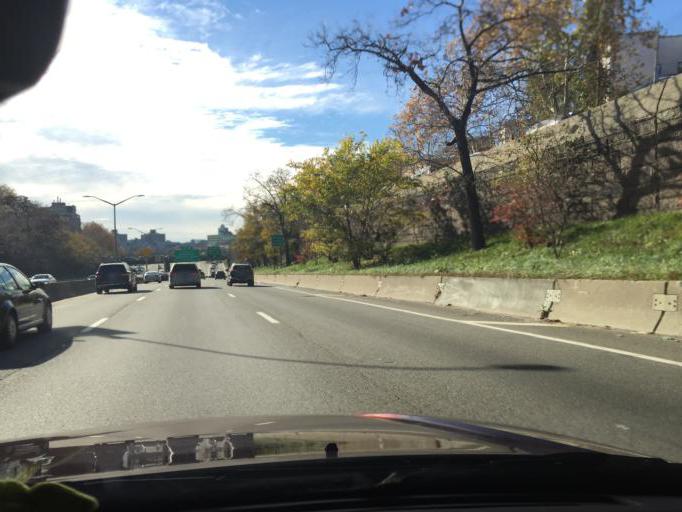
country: US
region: New York
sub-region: Queens County
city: Long Island City
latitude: 40.7052
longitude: -73.9592
